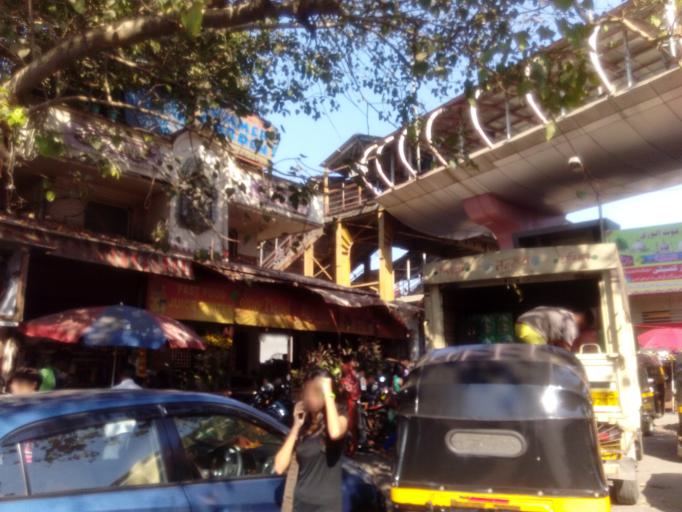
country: IN
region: Maharashtra
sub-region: Mumbai Suburban
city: Mumbai
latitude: 19.0824
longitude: 72.8412
